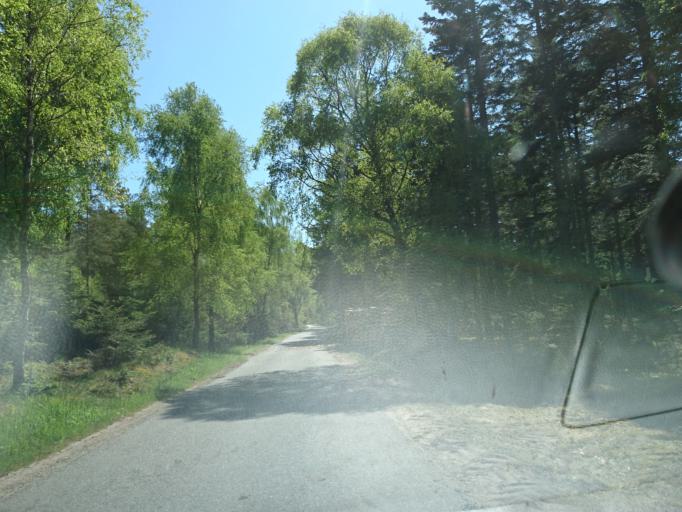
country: DK
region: North Denmark
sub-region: Hjorring Kommune
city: Sindal
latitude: 57.5941
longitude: 10.2293
